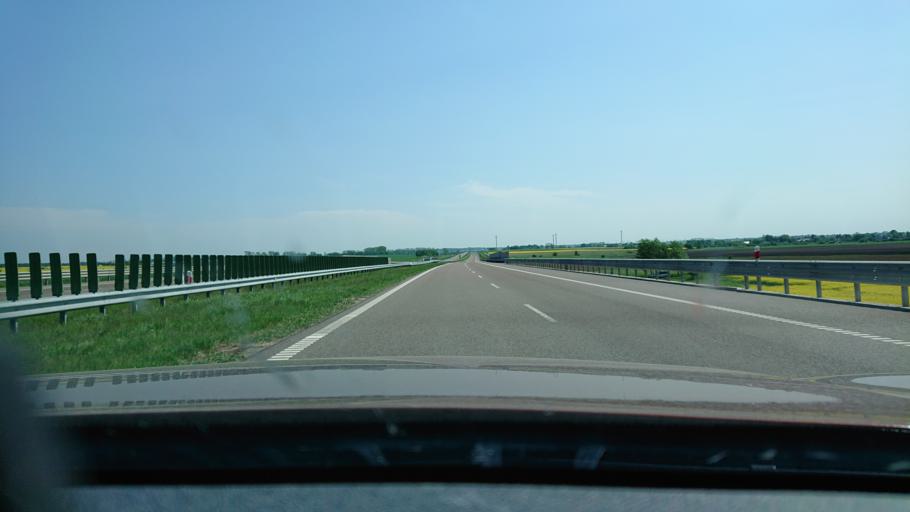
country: PL
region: Subcarpathian Voivodeship
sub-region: Powiat przemyski
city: Stubno
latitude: 49.9410
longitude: 22.9551
